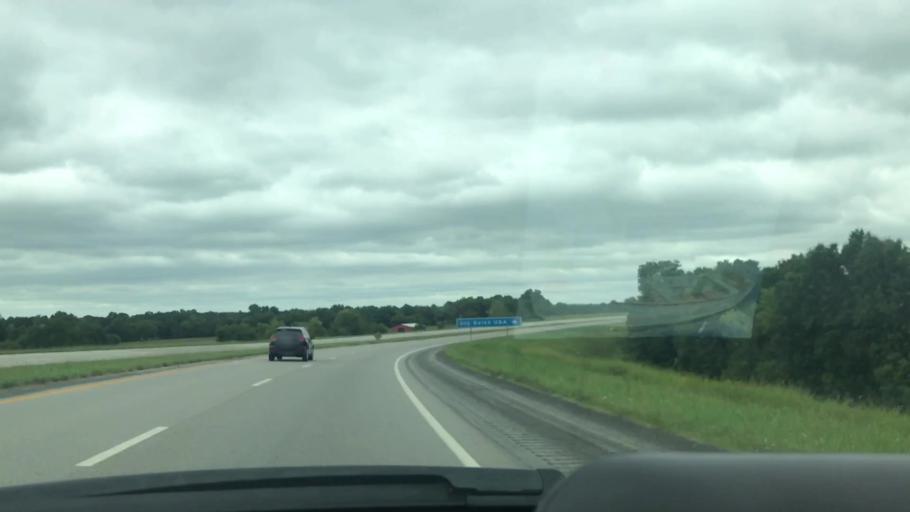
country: US
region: Oklahoma
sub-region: Mayes County
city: Pryor
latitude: 36.3751
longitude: -95.2961
